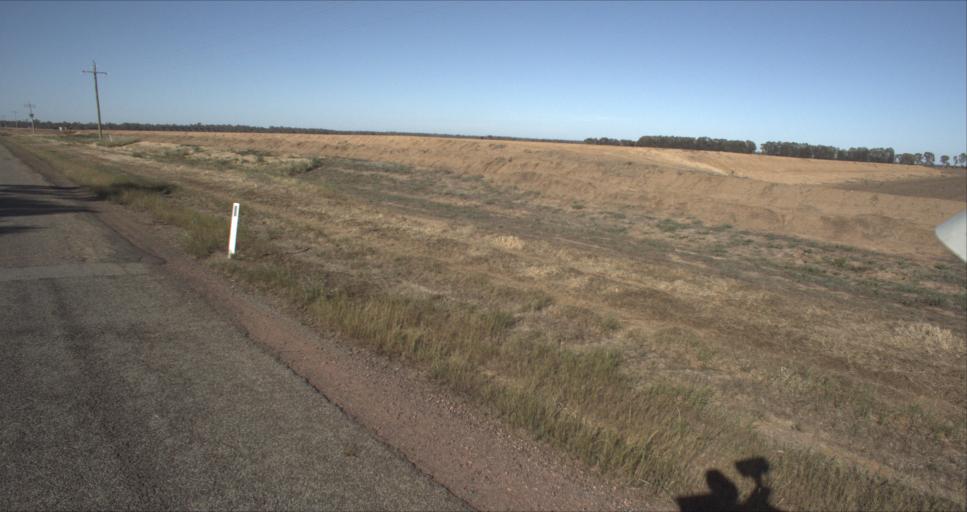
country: AU
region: New South Wales
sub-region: Leeton
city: Leeton
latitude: -34.5899
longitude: 146.2599
